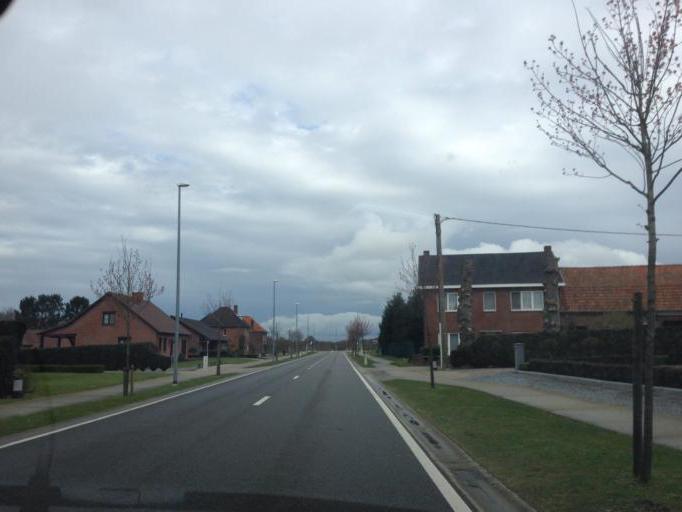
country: BE
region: Flanders
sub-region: Provincie Limburg
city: Bree
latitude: 51.1166
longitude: 5.5529
